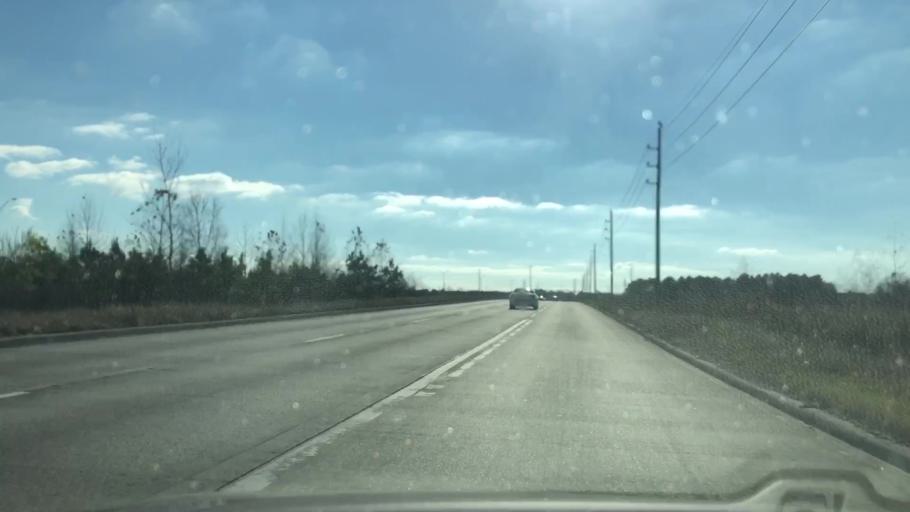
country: US
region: Texas
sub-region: Harris County
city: Cloverleaf
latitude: 29.8277
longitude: -95.1724
